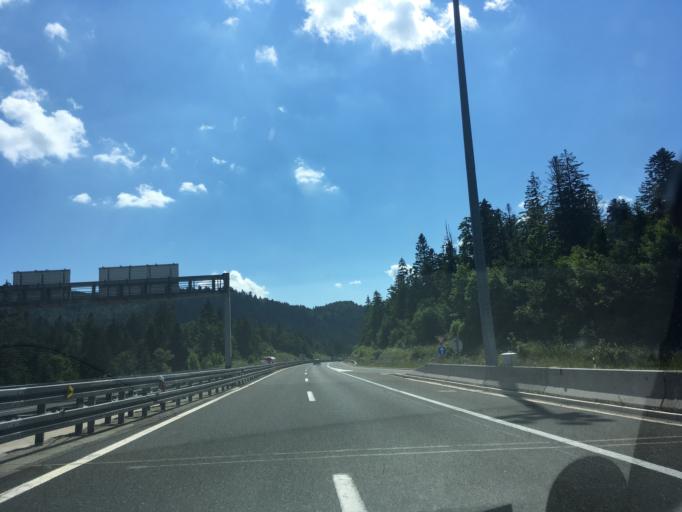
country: HR
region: Primorsko-Goranska
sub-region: Grad Delnice
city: Delnice
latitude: 45.3744
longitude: 14.7922
